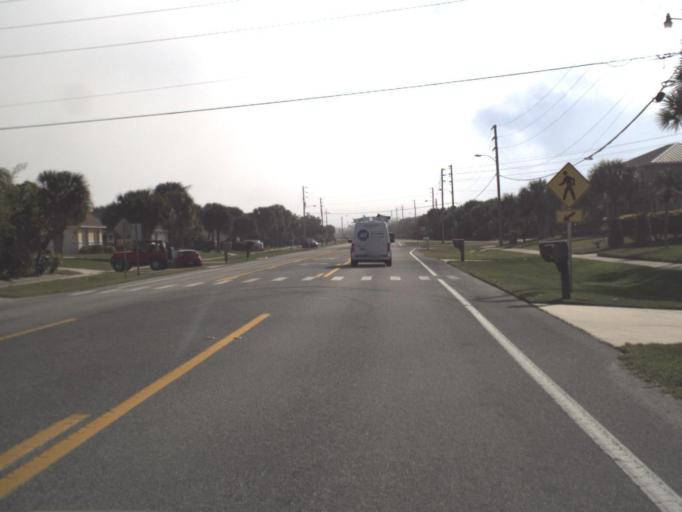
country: US
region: Florida
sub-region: Volusia County
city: Edgewater
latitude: 28.9853
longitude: -80.8645
